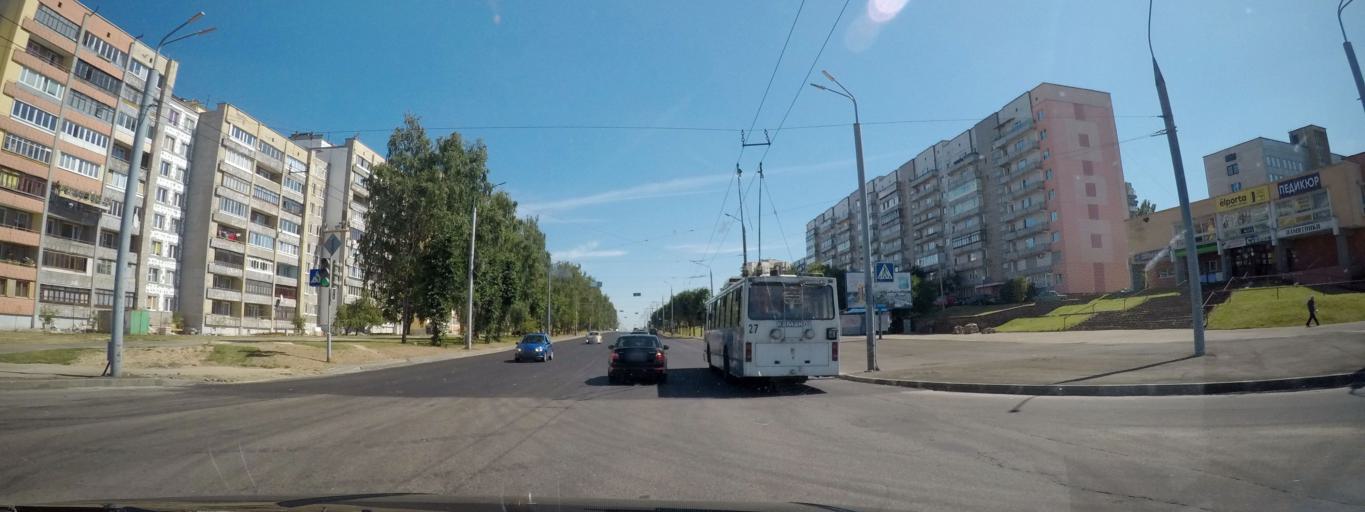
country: BY
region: Grodnenskaya
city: Hrodna
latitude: 53.6595
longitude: 23.8356
